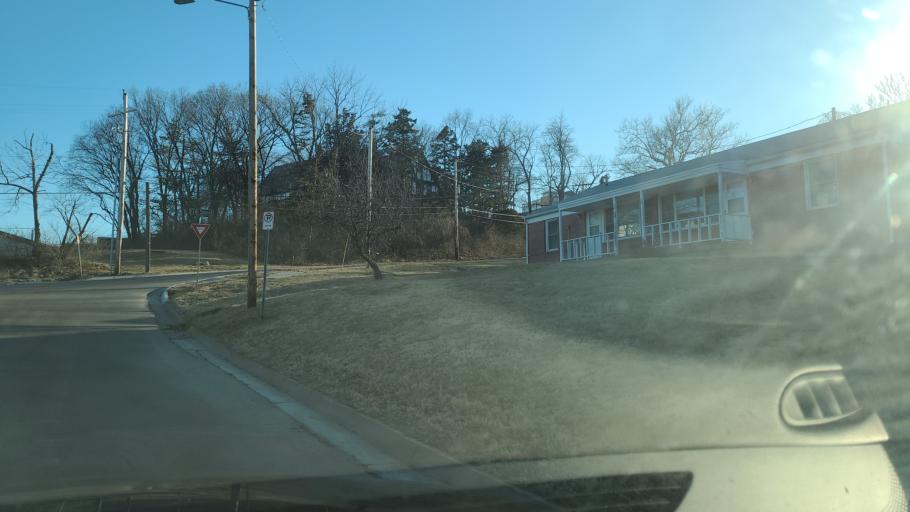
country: US
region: Kansas
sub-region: Douglas County
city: Lawrence
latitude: 38.9645
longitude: -95.2487
